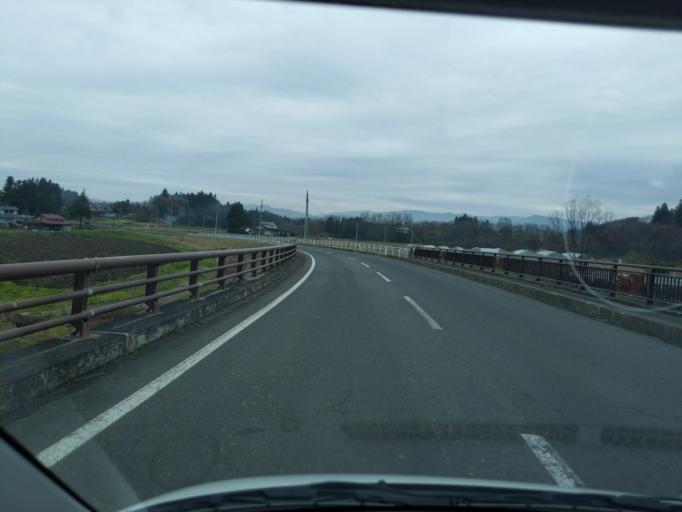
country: JP
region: Iwate
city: Mizusawa
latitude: 39.2152
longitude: 141.2247
